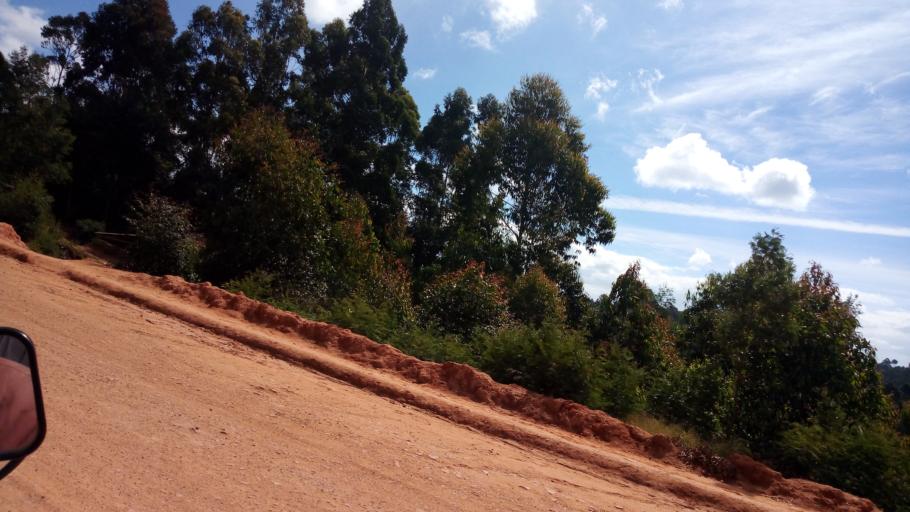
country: KE
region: Makueni
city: Wote
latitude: -1.6535
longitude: 37.4600
